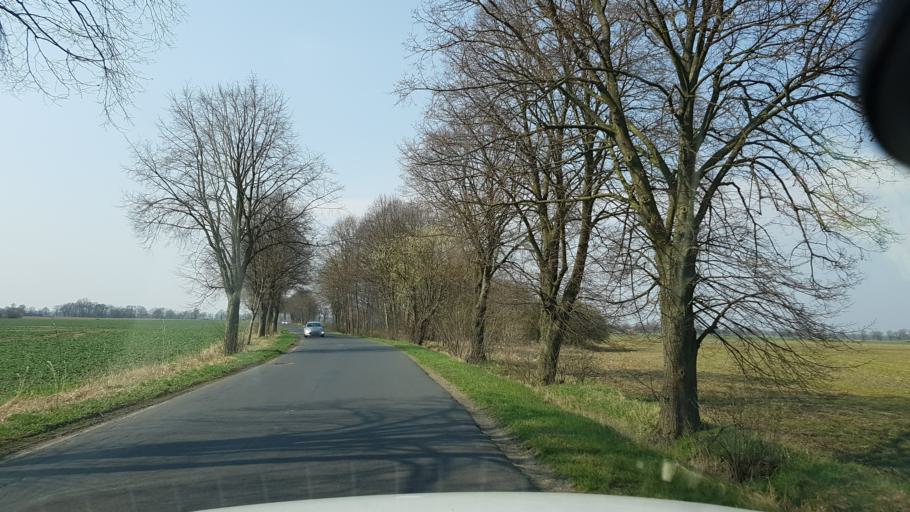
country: PL
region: West Pomeranian Voivodeship
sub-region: Powiat stargardzki
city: Stara Dabrowa
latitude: 53.3600
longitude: 15.1278
